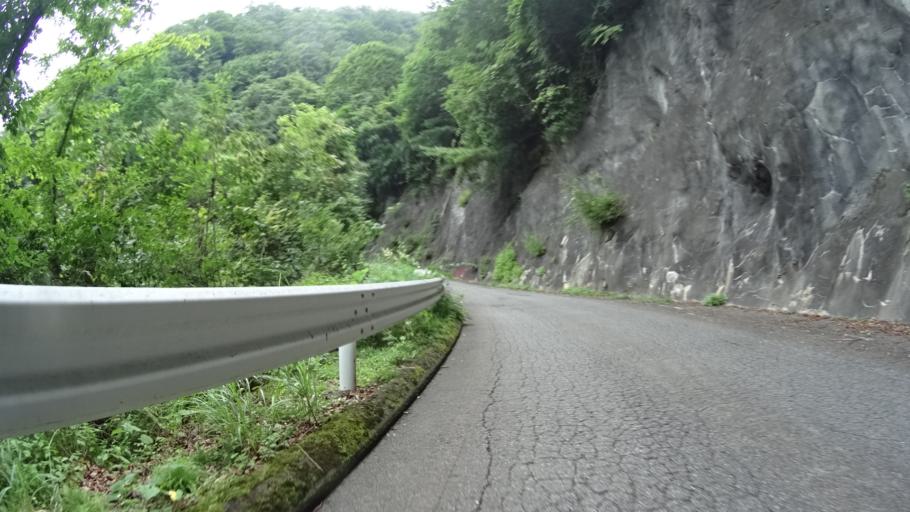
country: JP
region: Nagano
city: Saku
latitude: 36.0705
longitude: 138.6455
